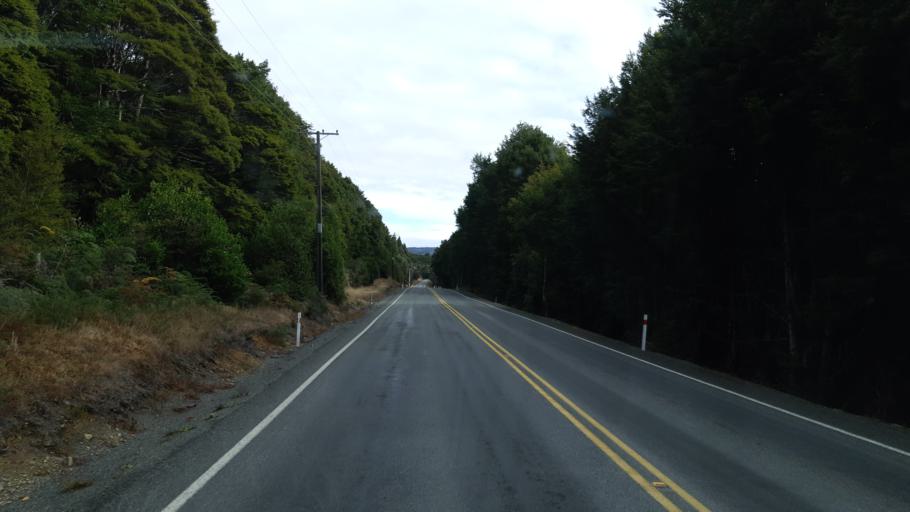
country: NZ
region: Tasman
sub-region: Tasman District
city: Wakefield
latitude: -41.7764
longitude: 172.9245
